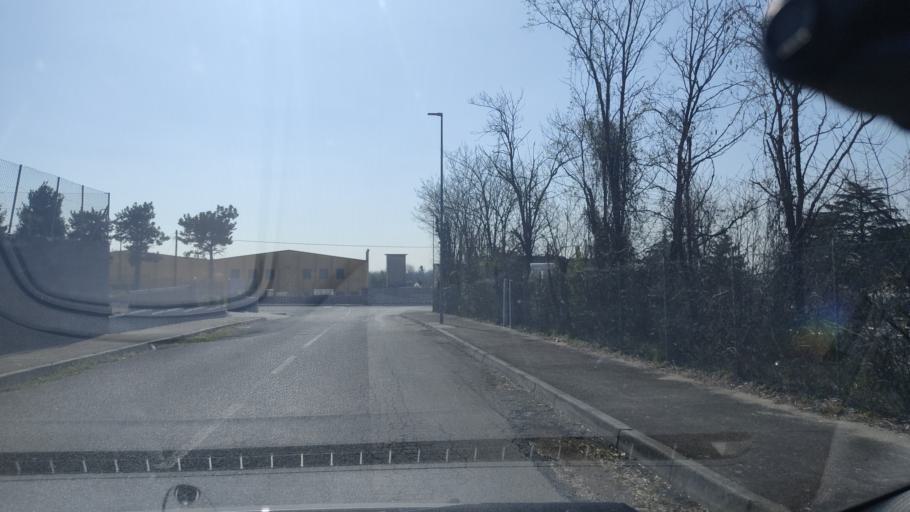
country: IT
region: Friuli Venezia Giulia
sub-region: Provincia di Pordenone
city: Budoia
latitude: 46.0385
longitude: 12.5498
